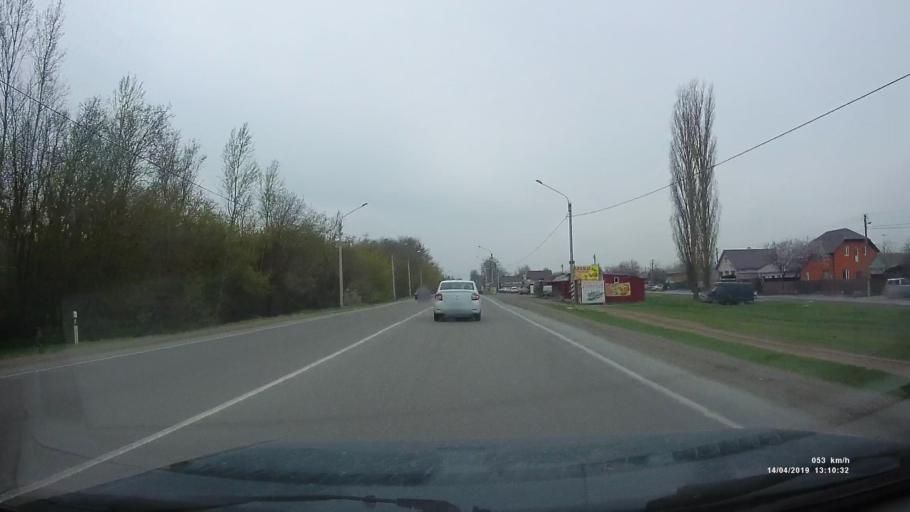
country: RU
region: Rostov
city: Kuleshovka
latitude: 47.1093
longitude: 39.6513
